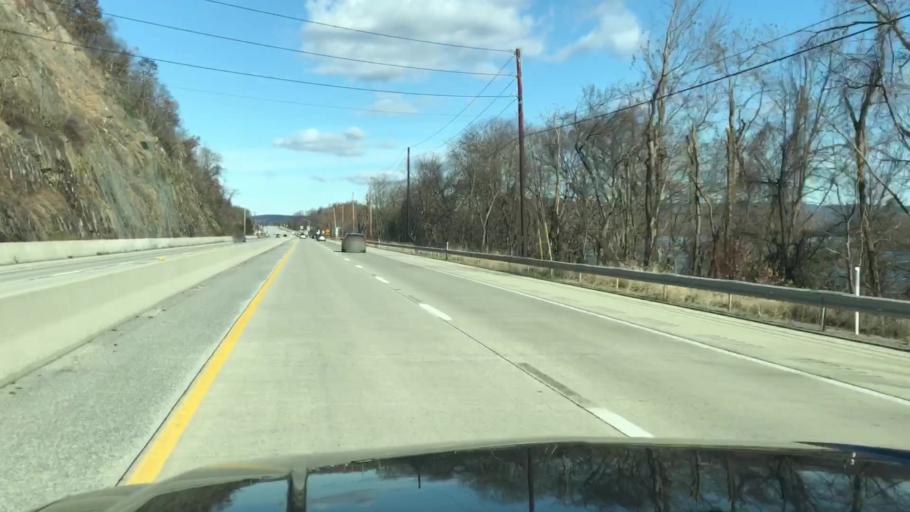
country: US
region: Pennsylvania
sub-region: Dauphin County
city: Millersburg
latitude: 40.5207
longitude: -76.9857
